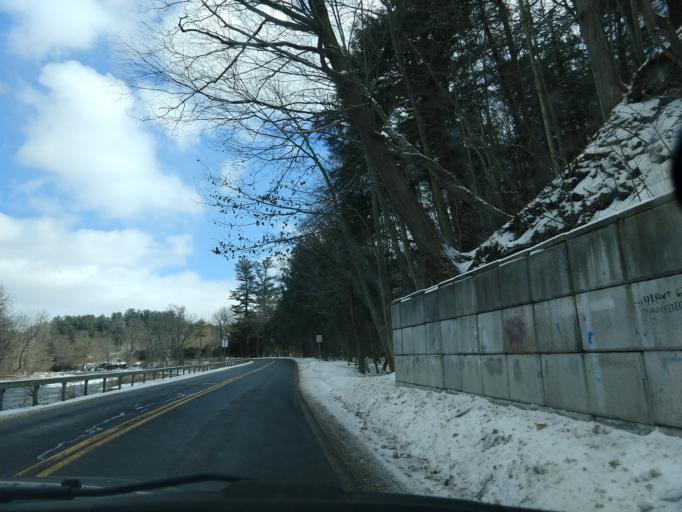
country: US
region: New York
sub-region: Tompkins County
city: Northeast Ithaca
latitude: 42.4531
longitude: -76.4609
